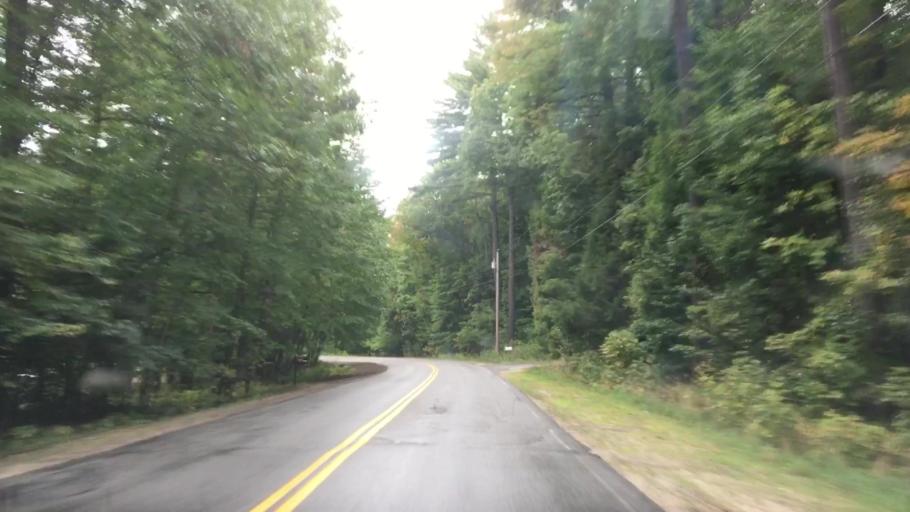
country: US
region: Maine
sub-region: Cumberland County
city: Raymond
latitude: 43.9336
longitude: -70.4122
